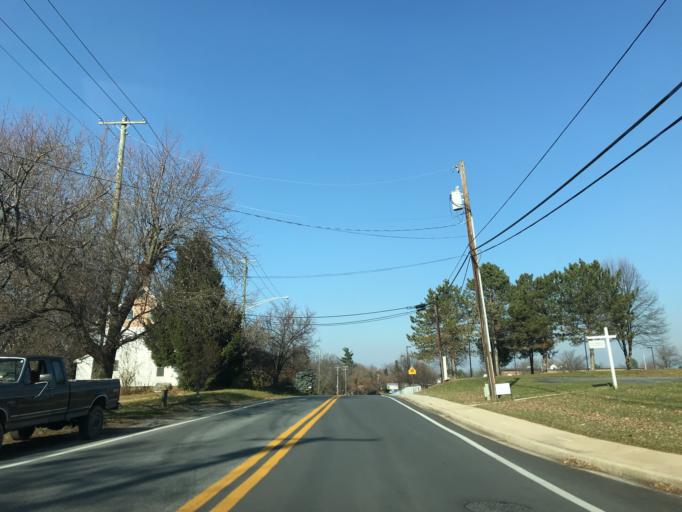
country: US
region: Maryland
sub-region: Carroll County
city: Taneytown
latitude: 39.6507
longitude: -77.1712
